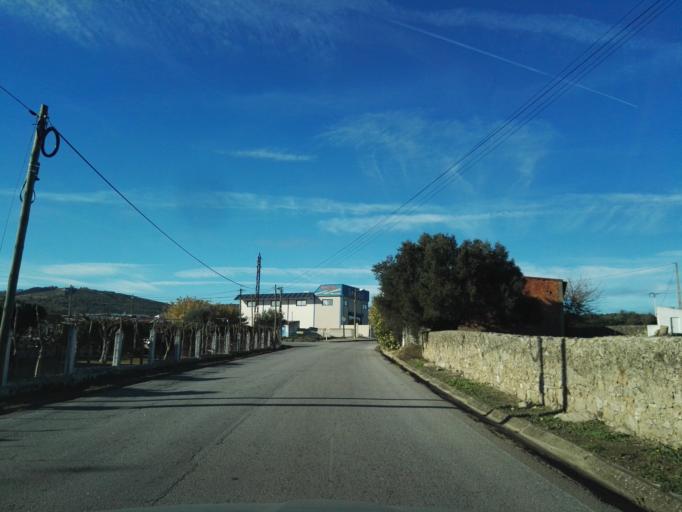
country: PT
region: Portalegre
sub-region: Elvas
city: Elvas
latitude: 38.8898
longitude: -7.1408
